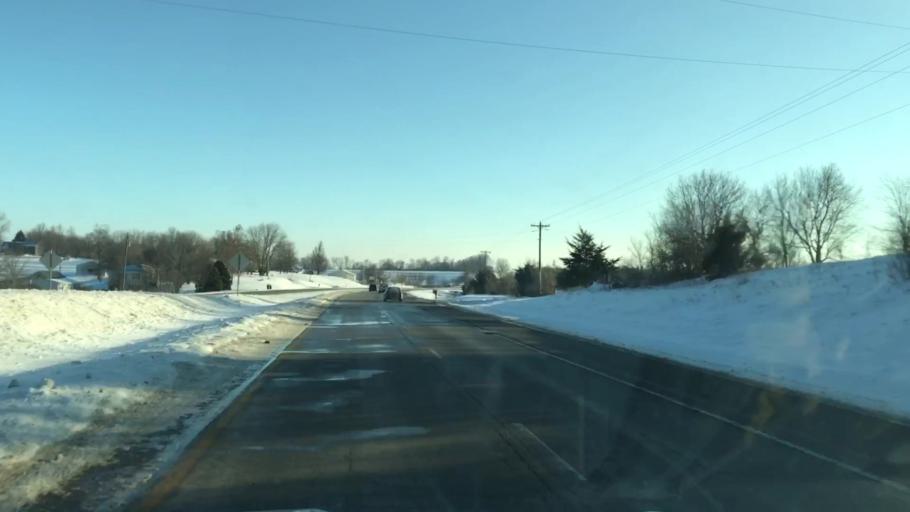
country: US
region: Missouri
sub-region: Andrew County
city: Country Club Village
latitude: 39.8693
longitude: -94.8085
